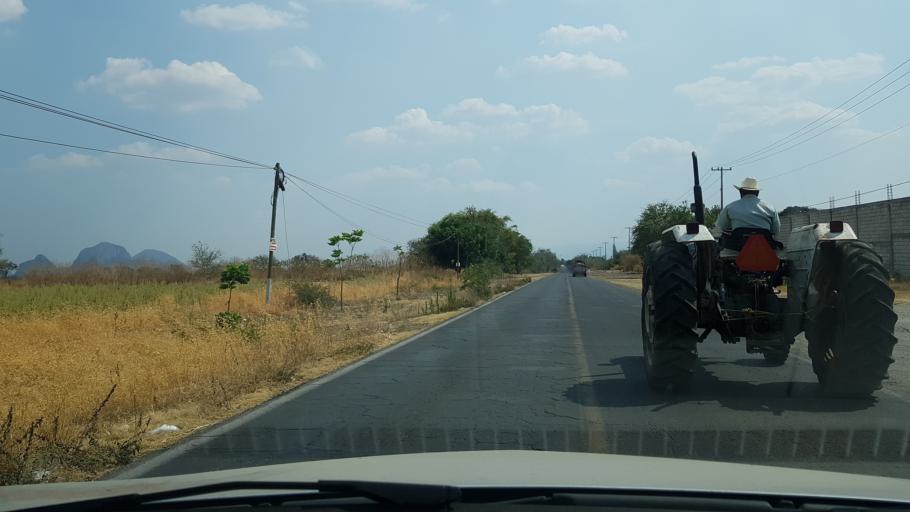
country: MX
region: Morelos
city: Amayuca
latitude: 18.7333
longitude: -98.7882
